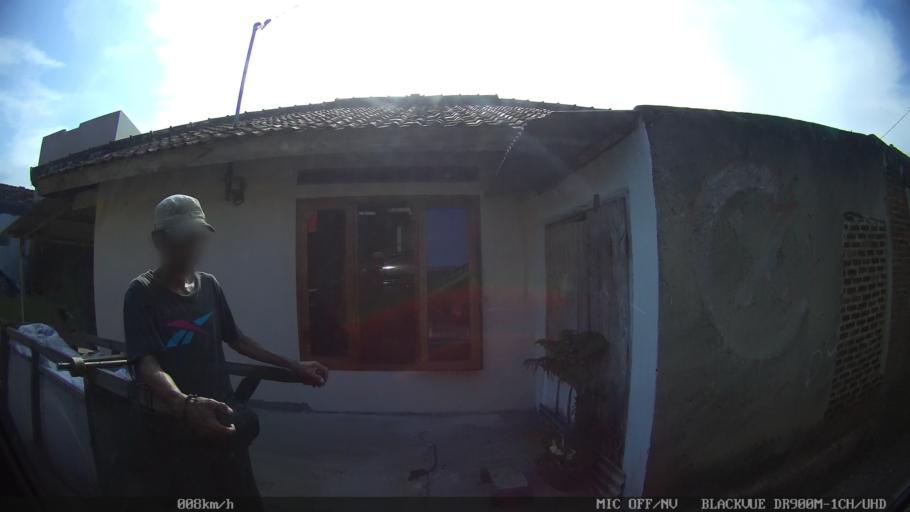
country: ID
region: Lampung
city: Kedaton
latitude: -5.3729
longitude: 105.2363
